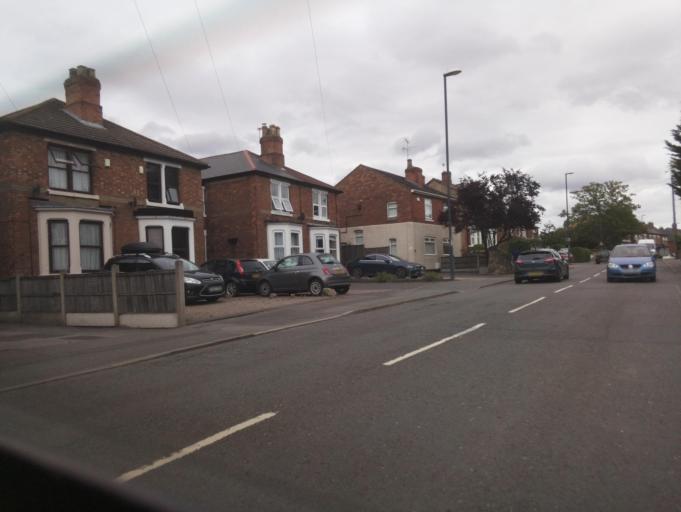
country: GB
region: England
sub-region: Derbyshire
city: Borrowash
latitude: 52.9137
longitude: -1.4066
